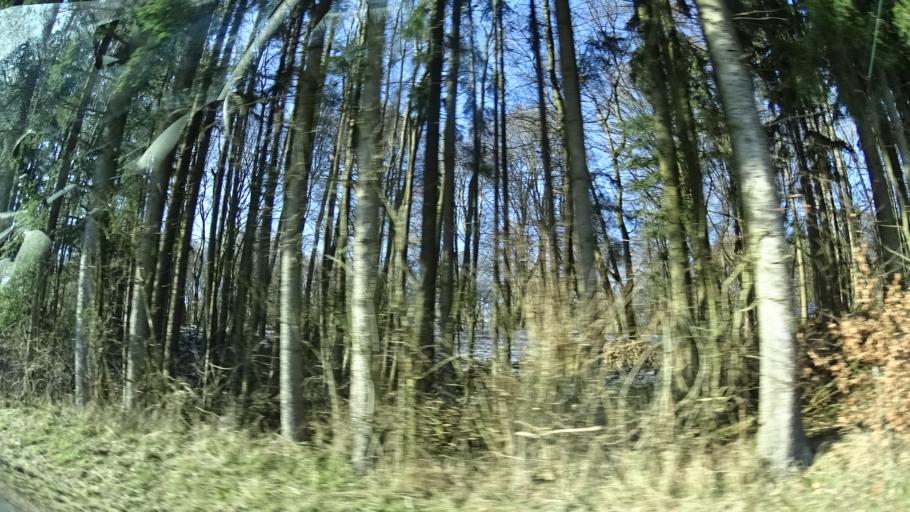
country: DE
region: Hesse
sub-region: Regierungsbezirk Kassel
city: Flieden
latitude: 50.3754
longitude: 9.5998
